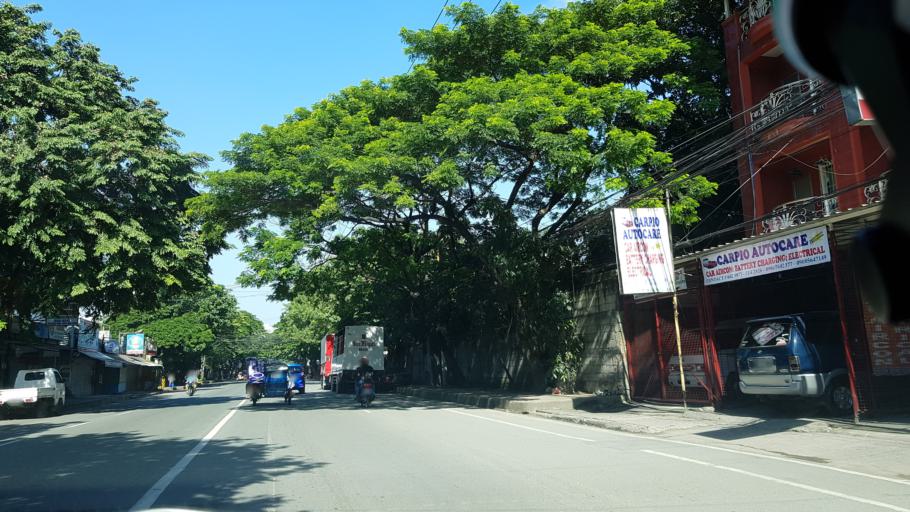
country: PH
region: Calabarzon
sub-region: Province of Rizal
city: Cainta
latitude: 14.5674
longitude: 121.0906
